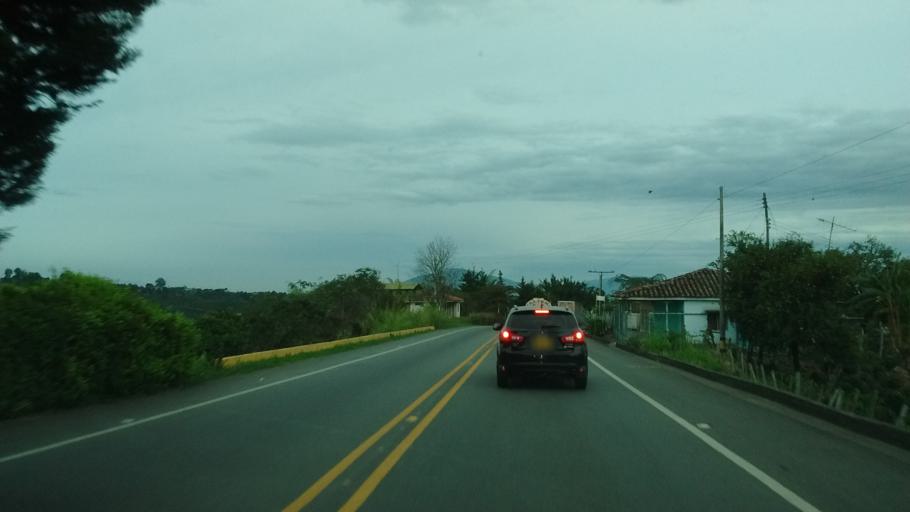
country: CO
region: Cauca
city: Morales
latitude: 2.7799
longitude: -76.5552
